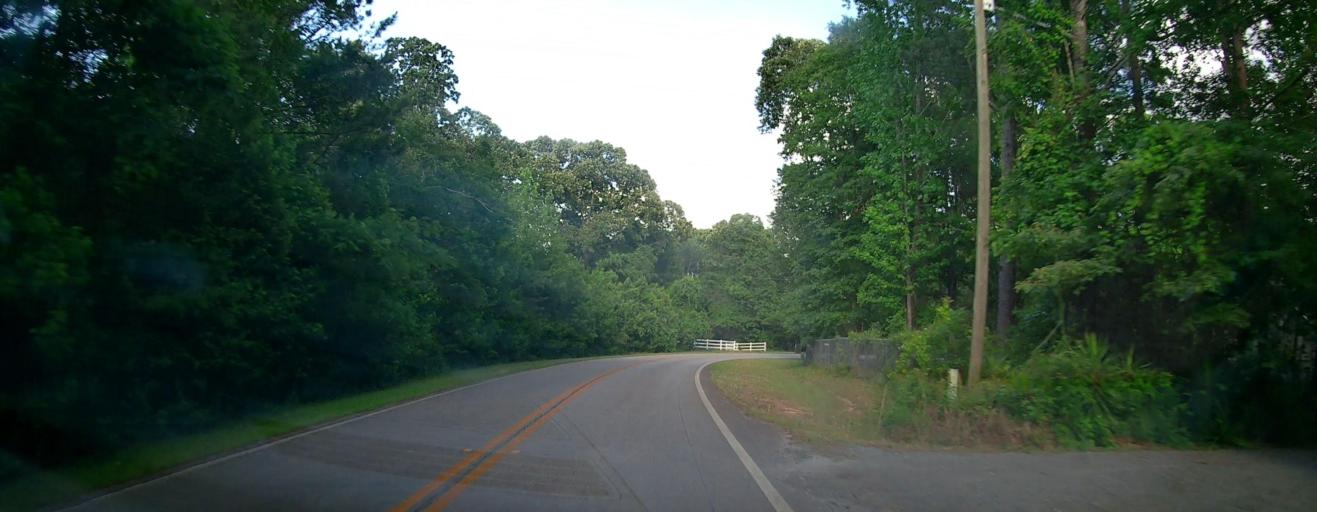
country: US
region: Georgia
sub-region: Peach County
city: Byron
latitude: 32.6600
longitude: -83.7926
